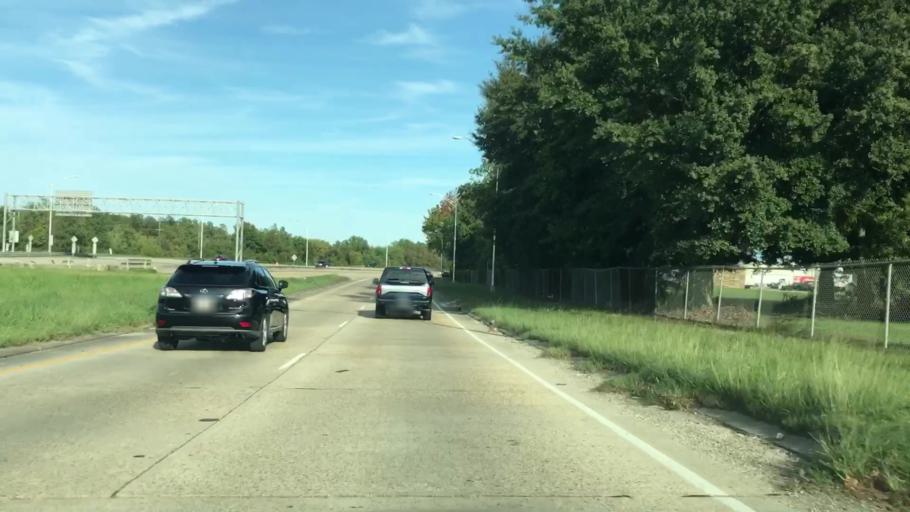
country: US
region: Louisiana
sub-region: Jefferson Parish
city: Elmwood
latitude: 29.9682
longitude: -90.1991
